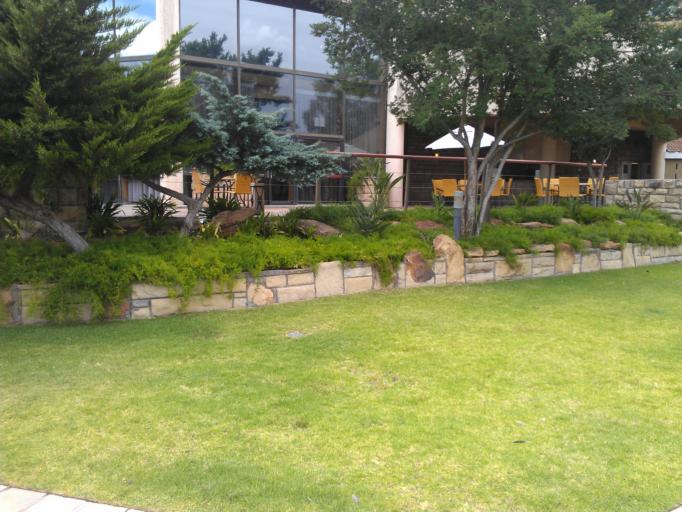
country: LS
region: Maseru
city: Maseru
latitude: -29.3179
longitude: 27.4885
